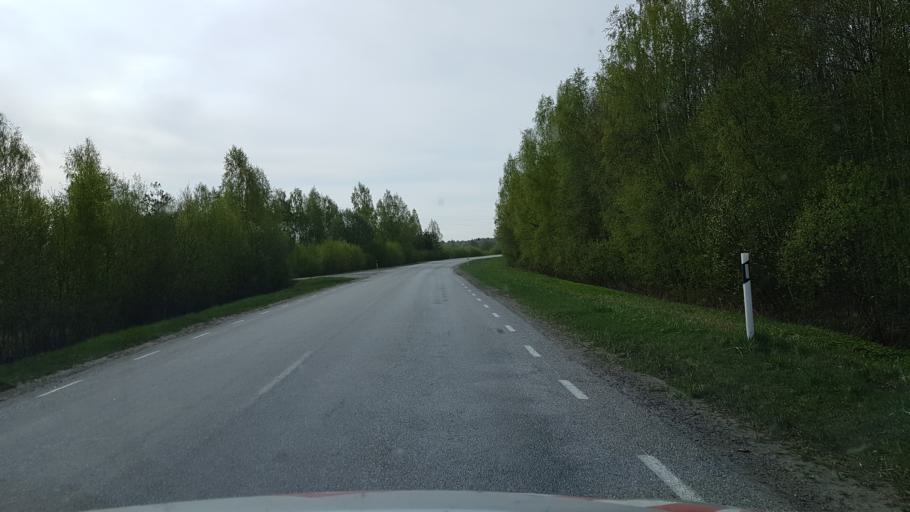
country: EE
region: Paernumaa
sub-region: Audru vald
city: Audru
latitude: 58.4202
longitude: 24.3097
